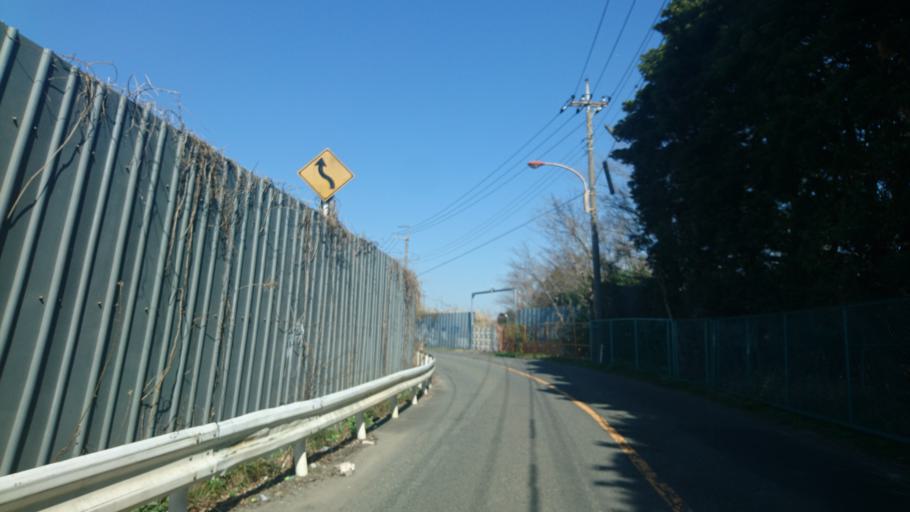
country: JP
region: Kanagawa
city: Fujisawa
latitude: 35.3968
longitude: 139.4483
